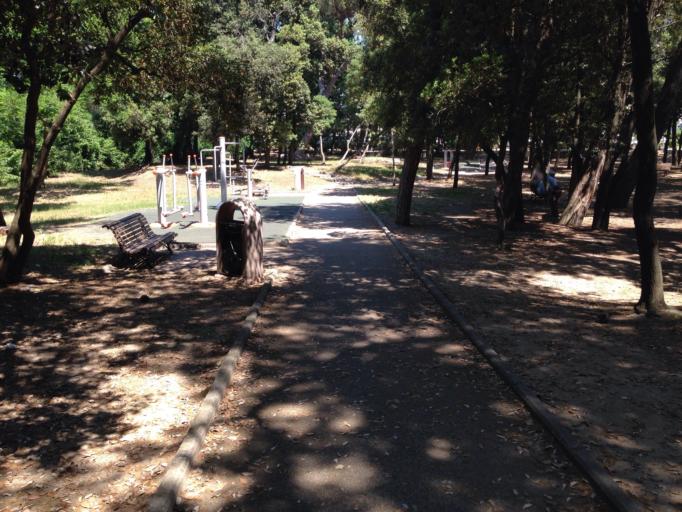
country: IT
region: Tuscany
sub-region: Province of Pisa
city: Marina di Pisa-Tirrenia-Calambrone
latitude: 43.6260
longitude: 10.2911
